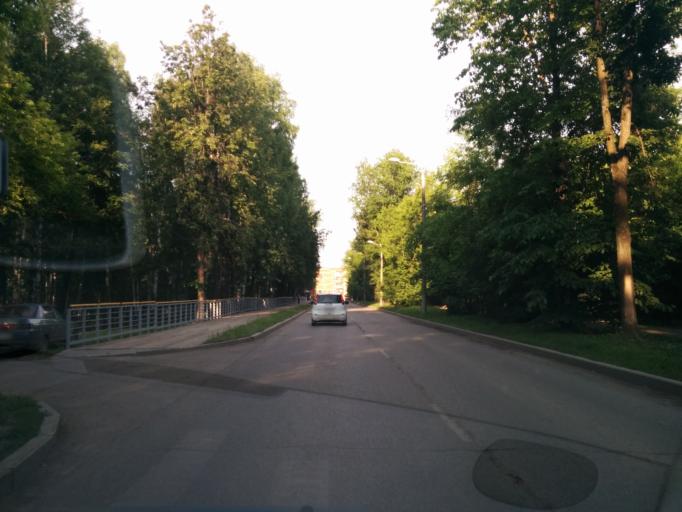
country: RU
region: Perm
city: Perm
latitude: 58.1121
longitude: 56.2995
